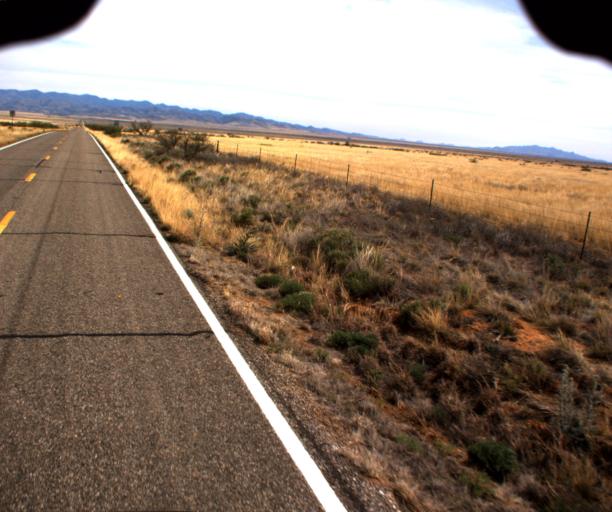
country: US
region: Arizona
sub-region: Cochise County
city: Willcox
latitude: 32.0914
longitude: -109.5322
